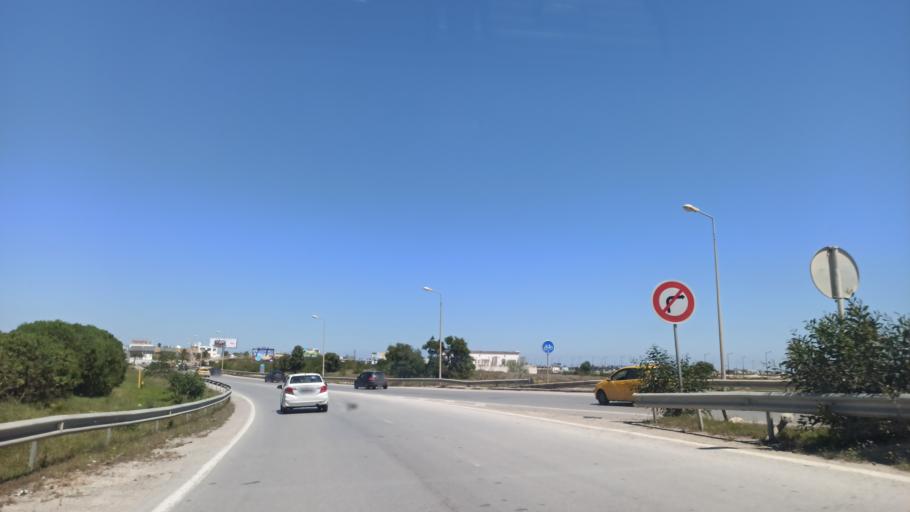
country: TN
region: Ariana
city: Ariana
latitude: 36.8253
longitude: 10.2022
